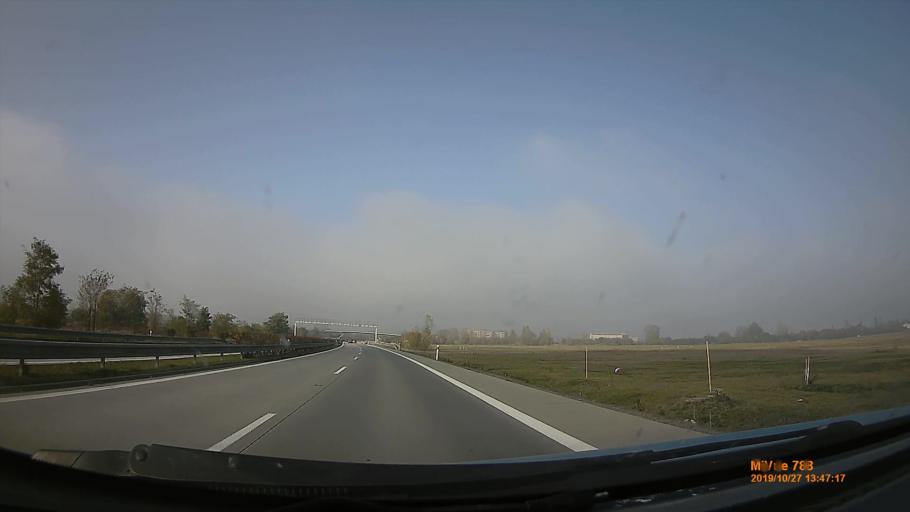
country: CZ
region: Olomoucky
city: Hnevotin
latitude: 49.5851
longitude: 17.2051
